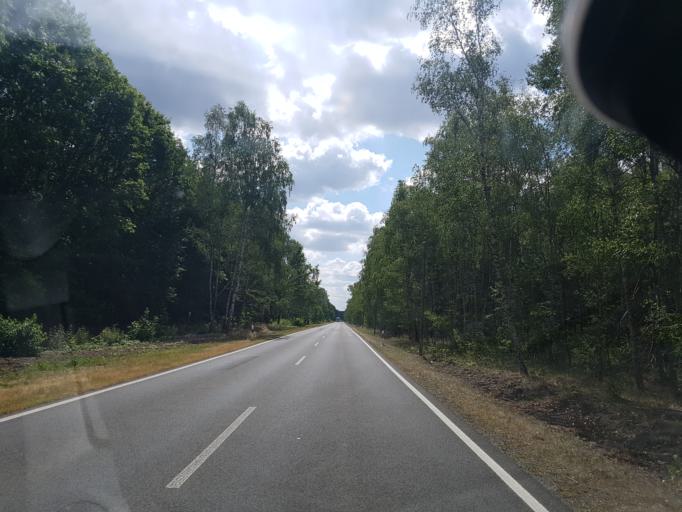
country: DE
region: Brandenburg
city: Drebkau
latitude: 51.6765
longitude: 14.1639
